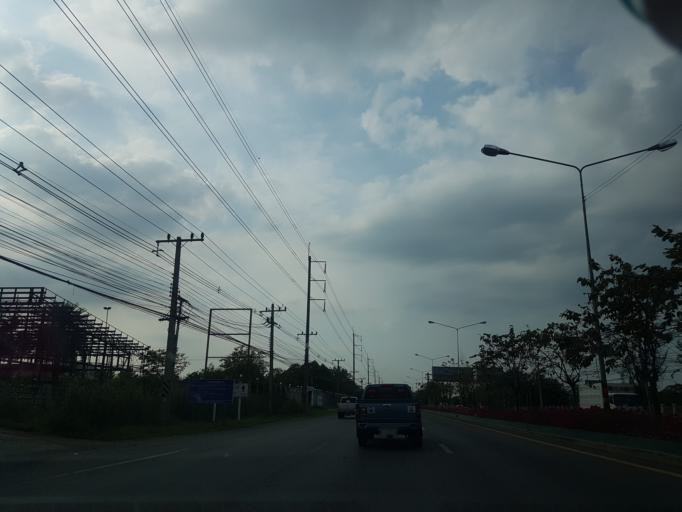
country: TH
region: Sara Buri
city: Phra Phutthabat
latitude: 14.7357
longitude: 100.7756
